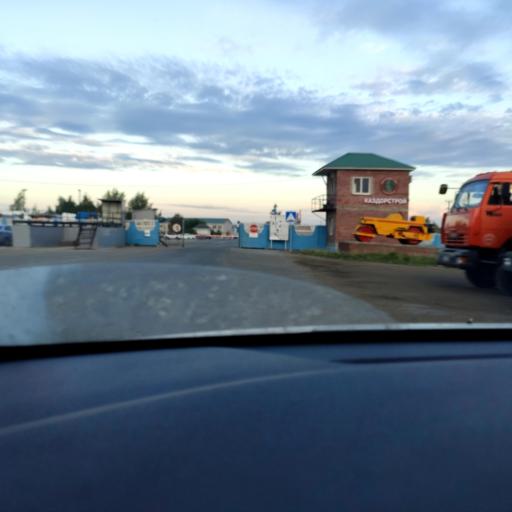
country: RU
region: Tatarstan
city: Staroye Arakchino
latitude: 55.8815
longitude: 48.9603
